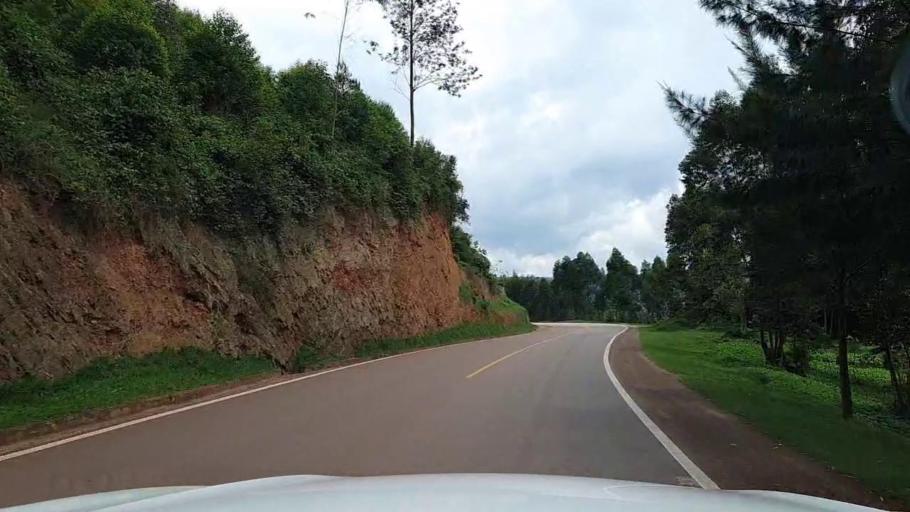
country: RW
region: Kigali
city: Kigali
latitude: -1.8160
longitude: 30.1182
